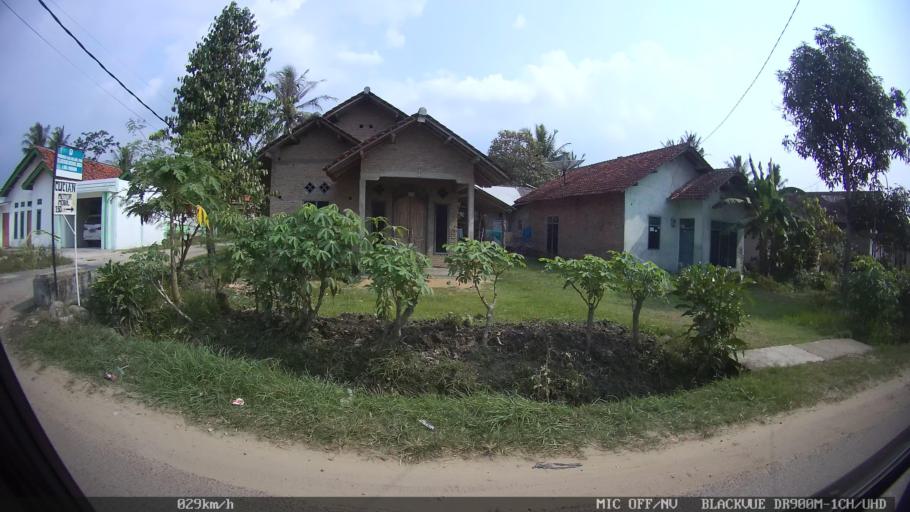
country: ID
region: Lampung
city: Kedondong
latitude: -5.4104
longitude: 104.9963
